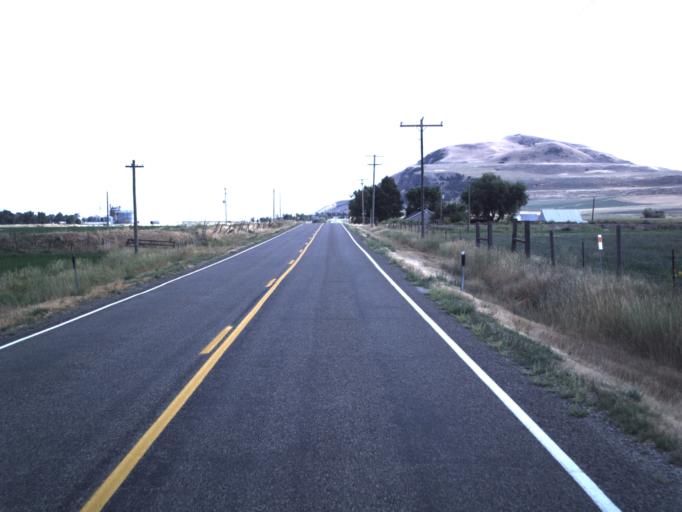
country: US
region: Utah
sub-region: Cache County
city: Lewiston
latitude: 41.9337
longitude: -111.9534
